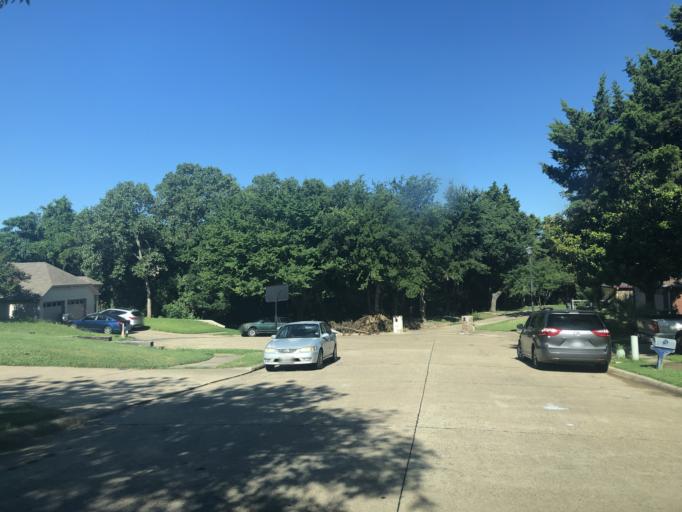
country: US
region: Texas
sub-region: Dallas County
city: Duncanville
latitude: 32.6684
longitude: -96.9355
